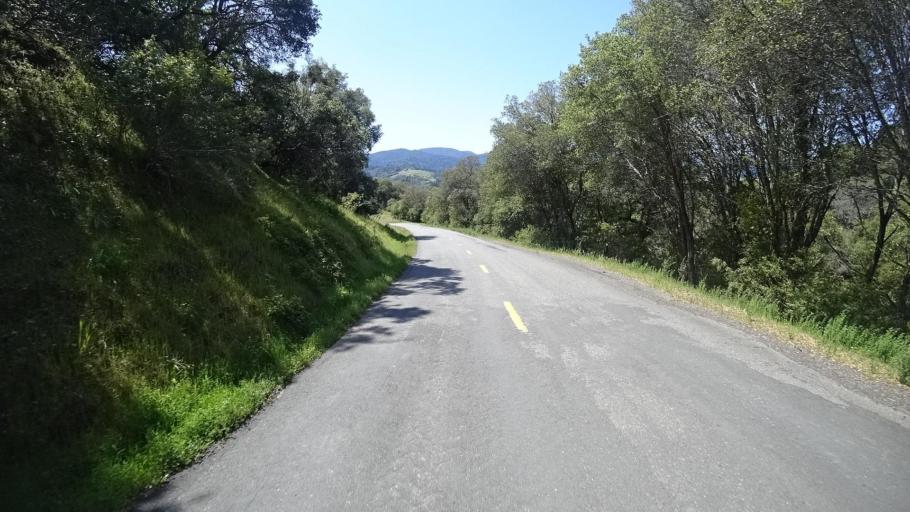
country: US
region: California
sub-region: Humboldt County
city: Redway
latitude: 40.1814
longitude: -123.5923
